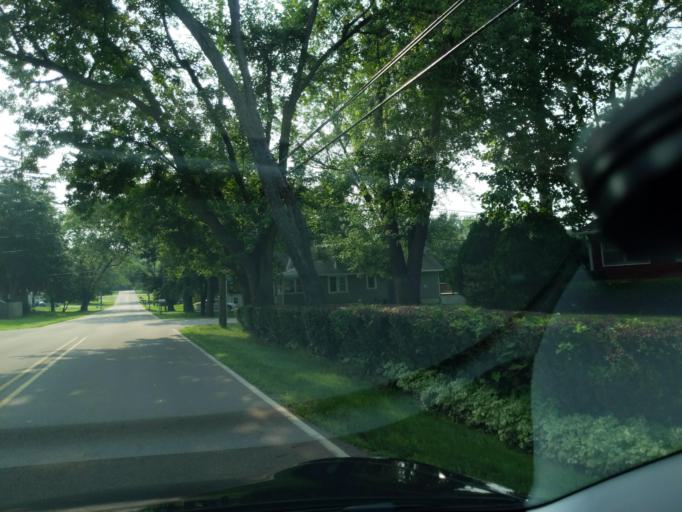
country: US
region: Michigan
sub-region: Jackson County
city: Jackson
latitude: 42.2400
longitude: -84.4389
